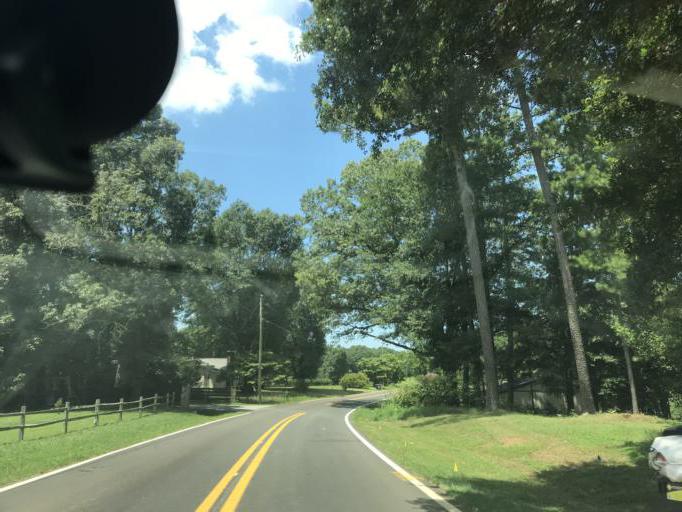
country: US
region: Georgia
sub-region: Forsyth County
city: Cumming
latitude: 34.2673
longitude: -84.2405
